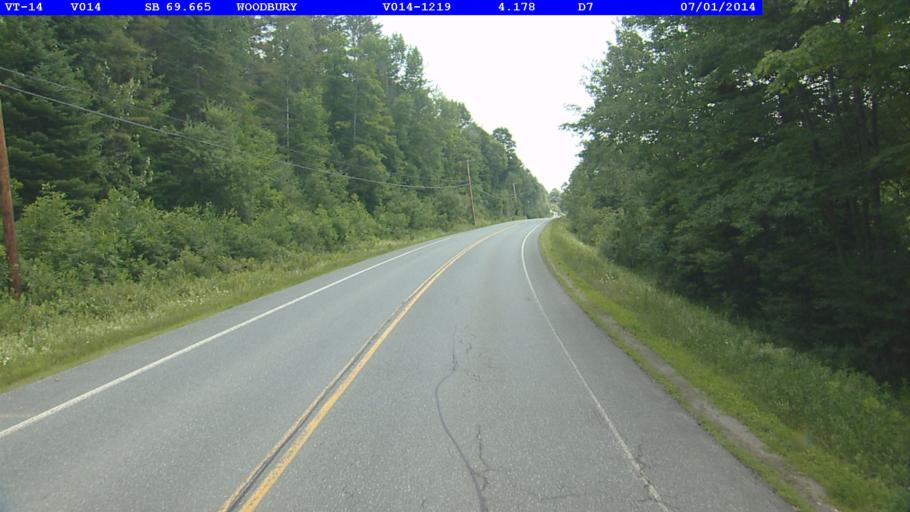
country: US
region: Vermont
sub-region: Caledonia County
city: Hardwick
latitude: 44.4481
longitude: -72.4168
